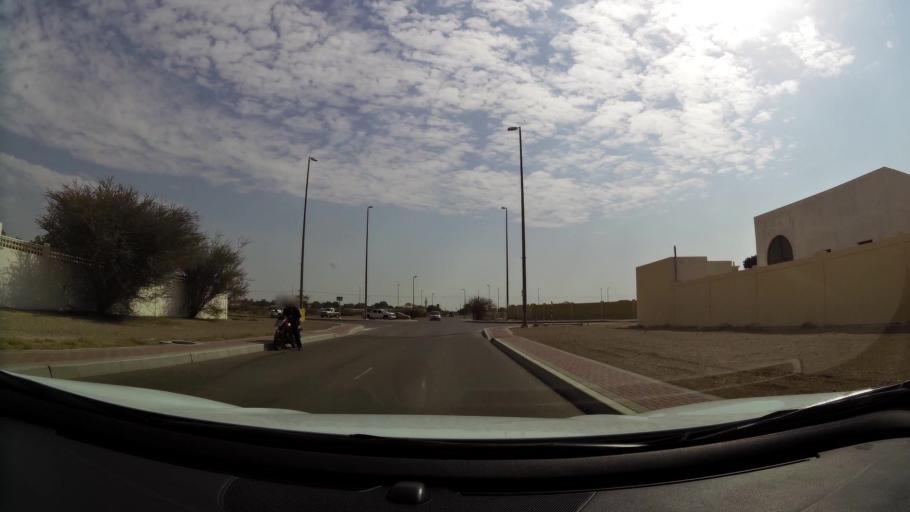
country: AE
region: Abu Dhabi
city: Al Ain
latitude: 24.0952
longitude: 55.9076
